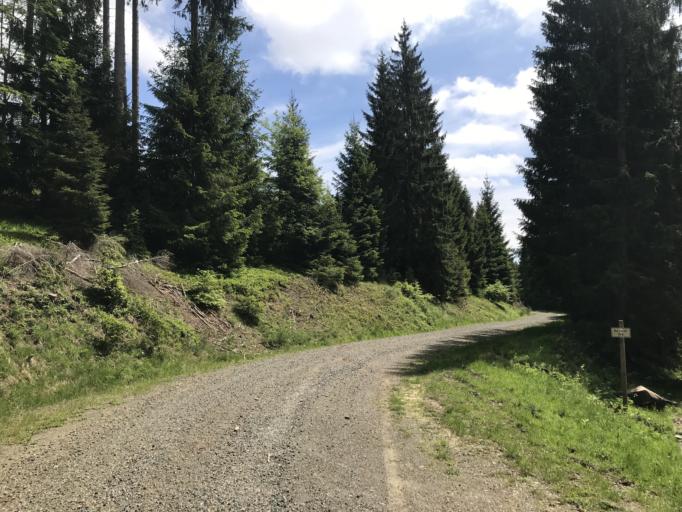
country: DE
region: Lower Saxony
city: Sankt Andreasberg
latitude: 51.7349
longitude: 10.4582
